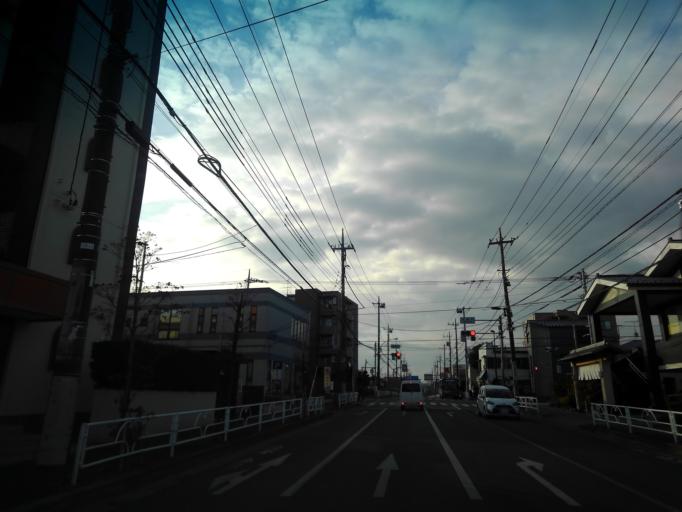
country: JP
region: Tokyo
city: Tanashicho
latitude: 35.7353
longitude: 139.5129
